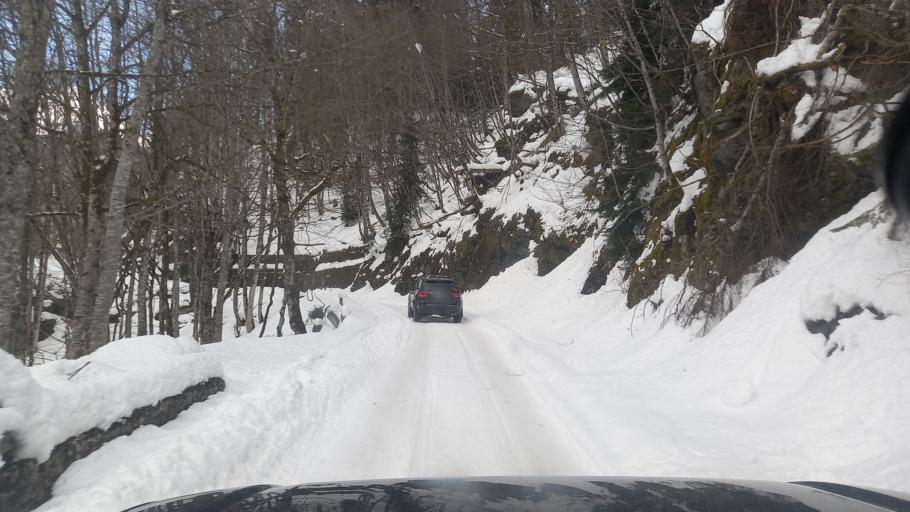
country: GE
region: Abkhazia
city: Gagra
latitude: 43.4767
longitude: 40.5421
